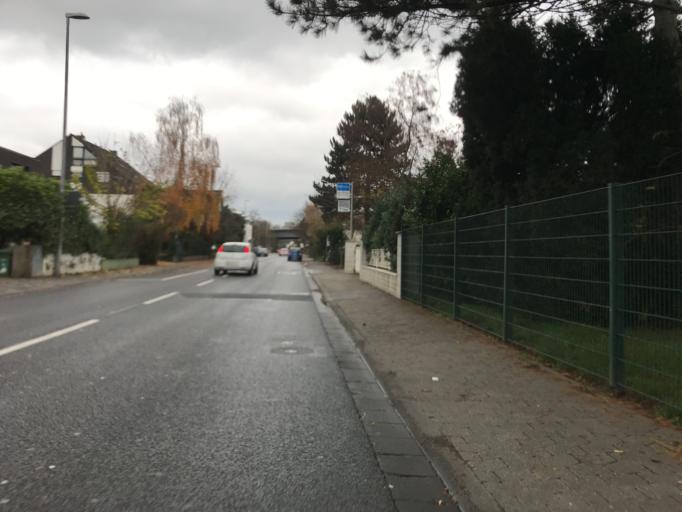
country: DE
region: Rheinland-Pfalz
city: Bodenheim
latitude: 49.9661
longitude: 8.3142
